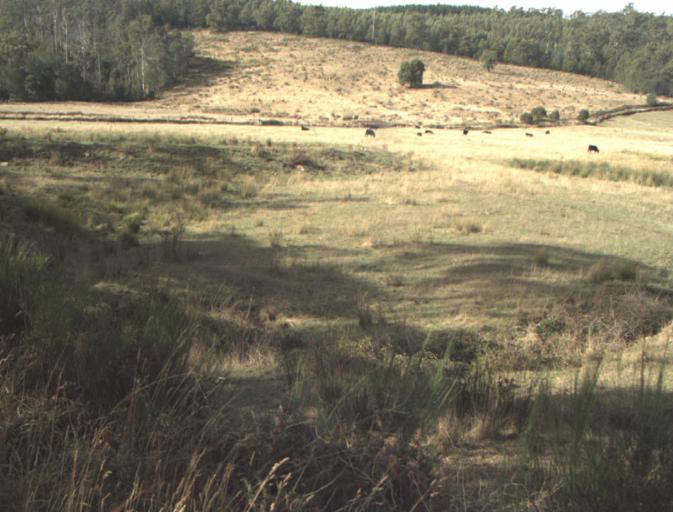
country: AU
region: Tasmania
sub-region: Launceston
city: Mayfield
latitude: -41.2098
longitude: 147.1498
